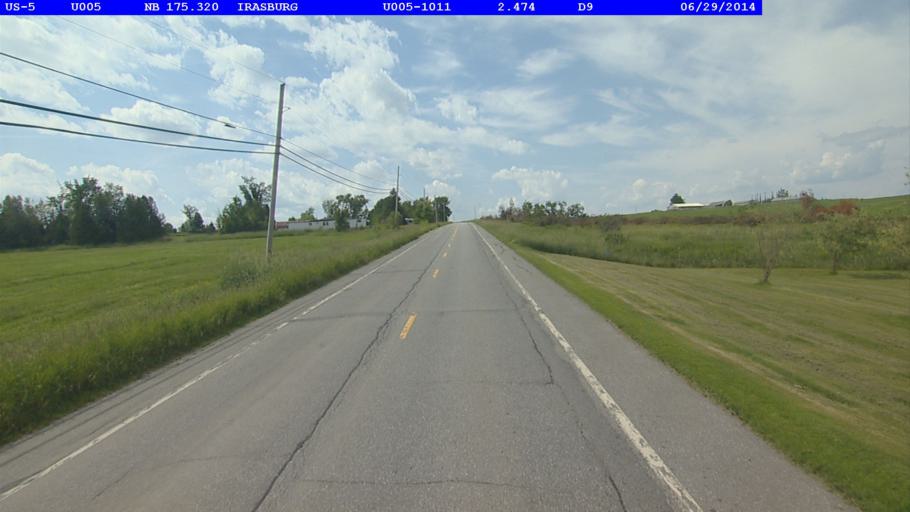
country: US
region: Vermont
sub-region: Orleans County
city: Newport
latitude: 44.8318
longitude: -72.2472
